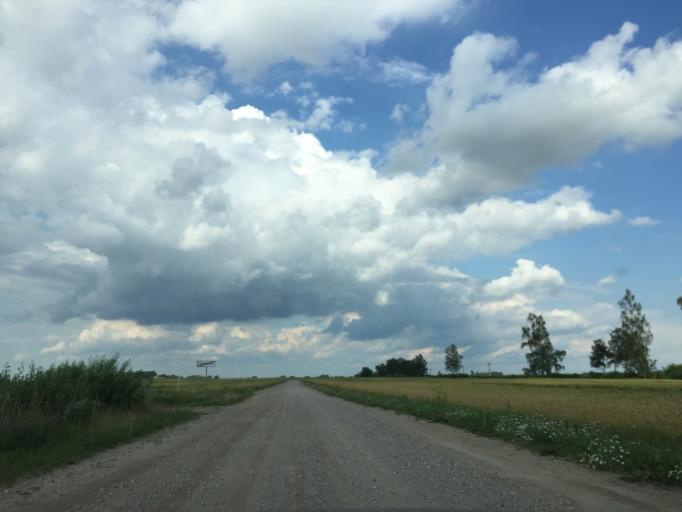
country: LV
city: Tervete
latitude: 56.5717
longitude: 23.3914
